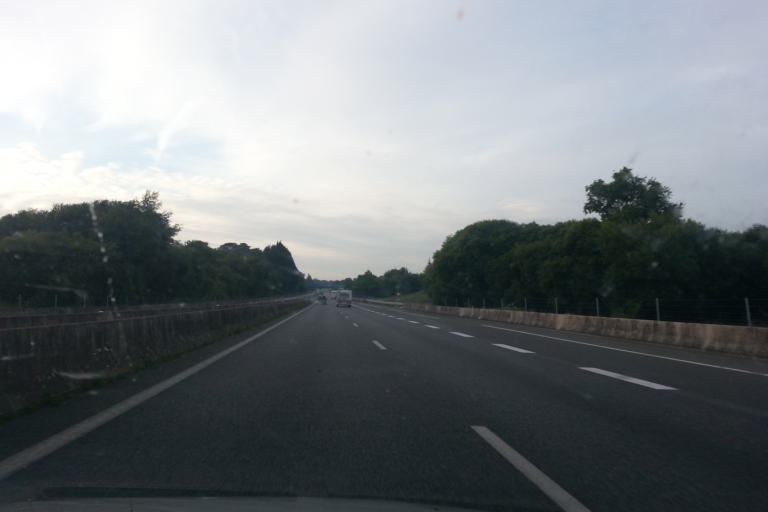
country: FR
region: Brittany
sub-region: Departement du Morbihan
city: Cleguer
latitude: 47.8510
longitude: -3.3417
